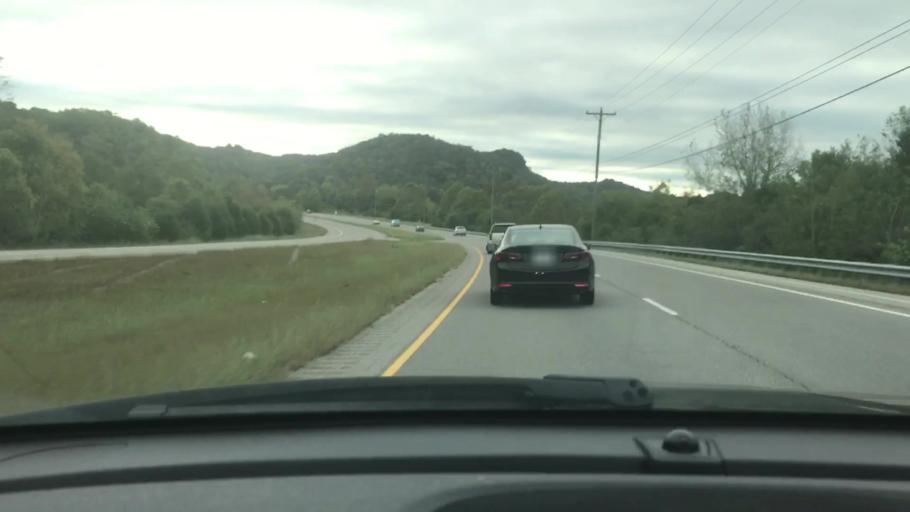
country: US
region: Tennessee
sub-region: Cheatham County
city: Ashland City
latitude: 36.2069
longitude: -86.9516
